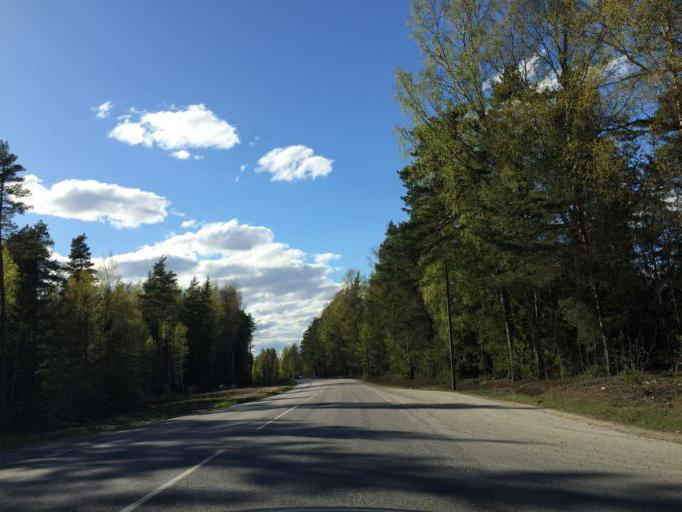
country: SE
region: Soedermanland
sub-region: Eskilstuna Kommun
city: Hallbybrunn
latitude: 59.4043
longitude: 16.3888
